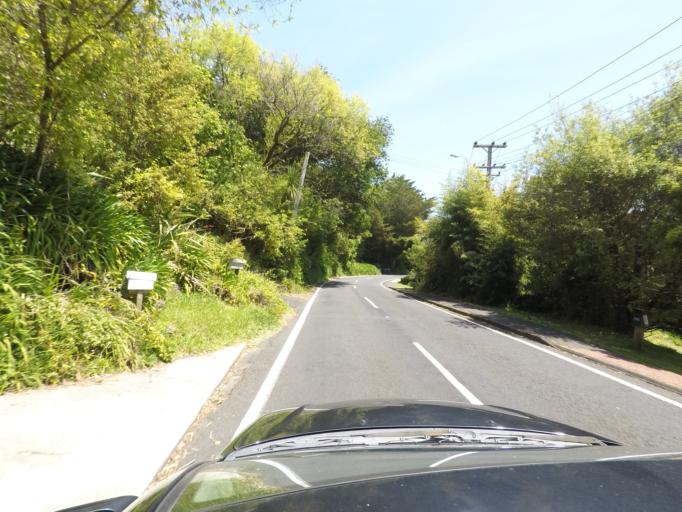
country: NZ
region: Auckland
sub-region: Auckland
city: Titirangi
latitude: -36.9691
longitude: 174.6374
